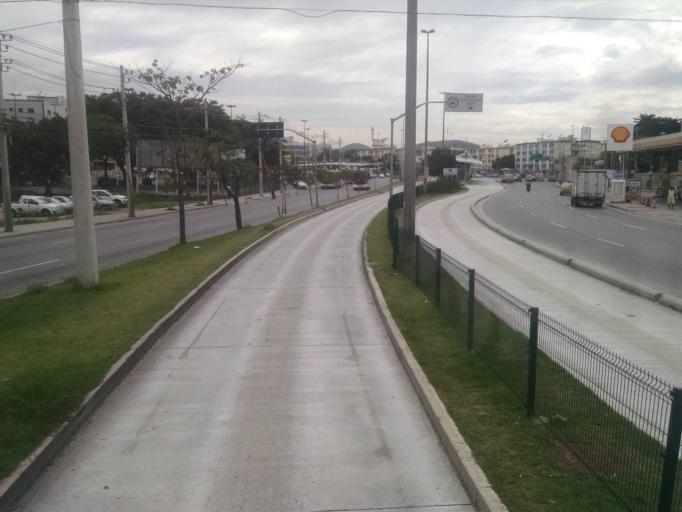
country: BR
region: Rio de Janeiro
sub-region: Sao Joao De Meriti
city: Sao Joao de Meriti
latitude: -22.9382
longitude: -43.3723
